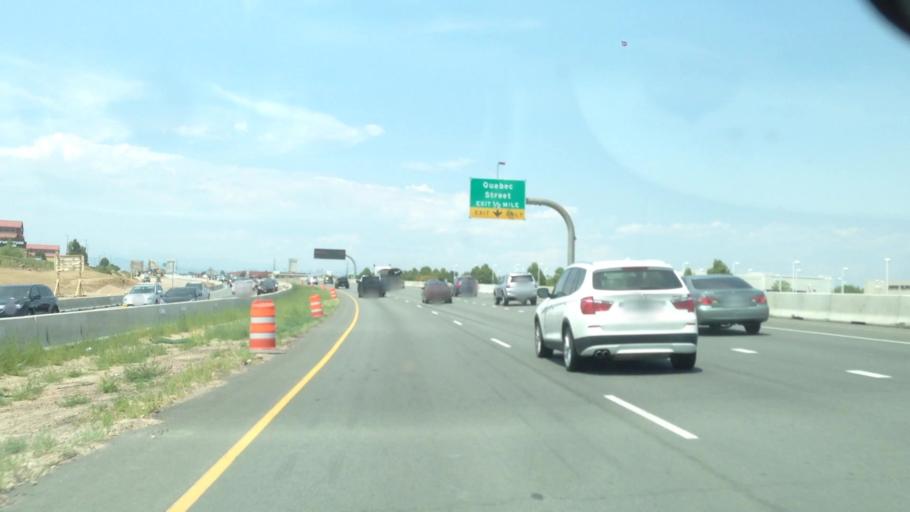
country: US
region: Colorado
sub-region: Douglas County
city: Acres Green
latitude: 39.5640
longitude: -104.8898
